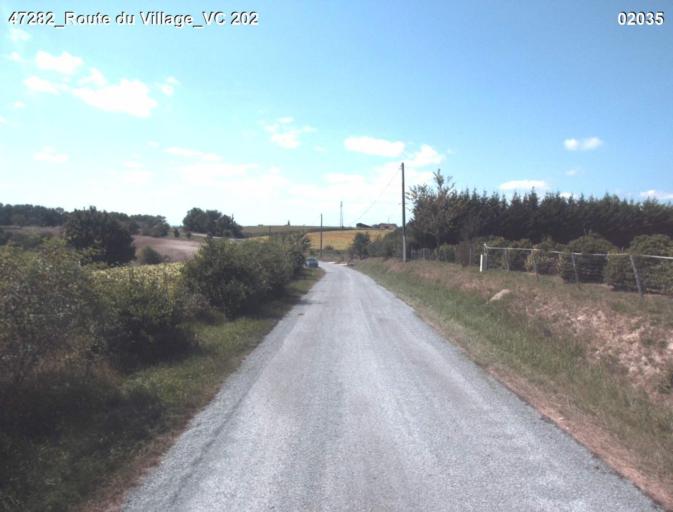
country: FR
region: Aquitaine
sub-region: Departement du Lot-et-Garonne
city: Laplume
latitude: 44.0890
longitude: 0.5224
